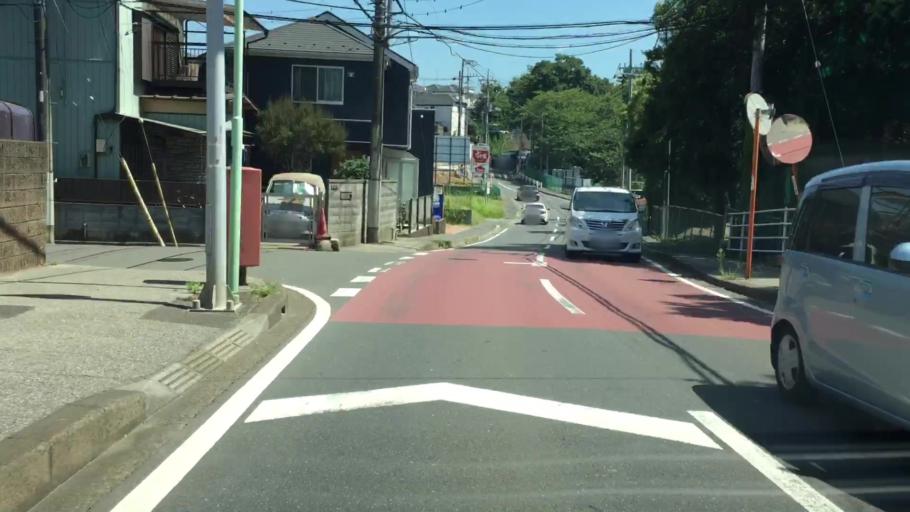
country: JP
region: Chiba
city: Funabashi
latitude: 35.7327
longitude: 139.9837
